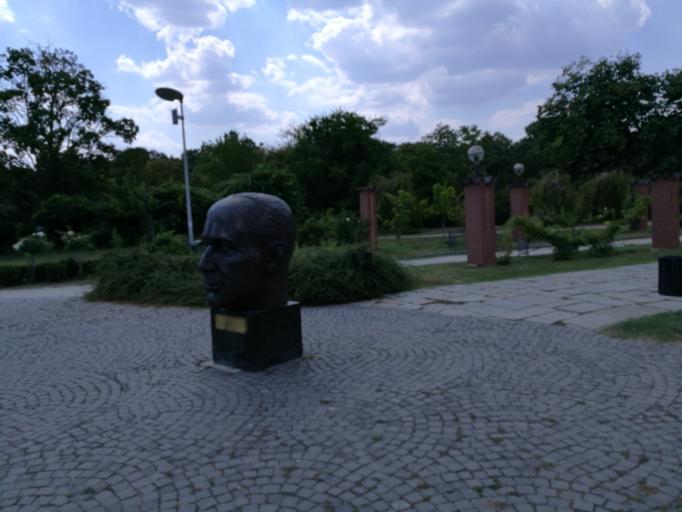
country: RO
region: Bucuresti
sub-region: Municipiul Bucuresti
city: Bucuresti
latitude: 44.4731
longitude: 26.0789
